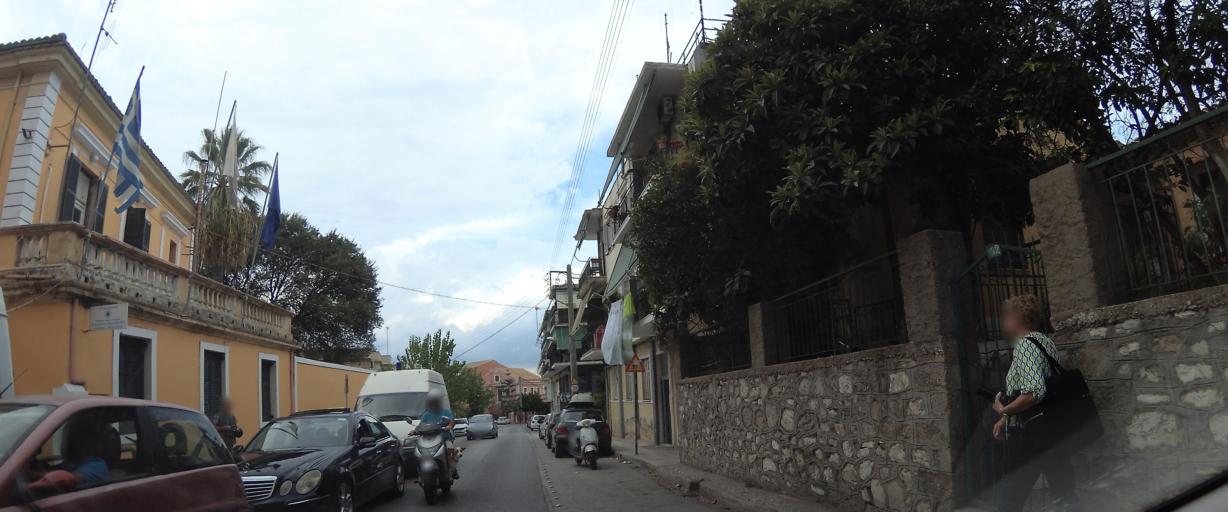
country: GR
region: Ionian Islands
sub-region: Nomos Kerkyras
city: Kerkyra
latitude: 39.6228
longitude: 19.9100
